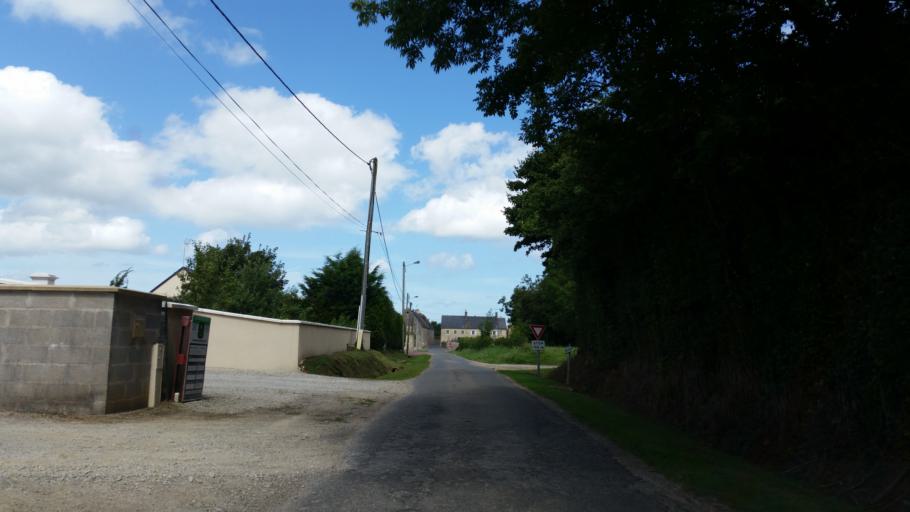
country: FR
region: Lower Normandy
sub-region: Departement de la Manche
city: Montebourg
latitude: 49.4575
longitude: -1.3440
